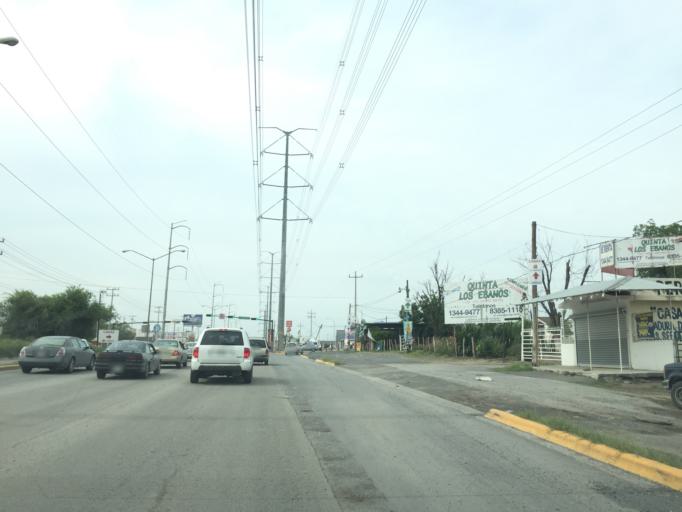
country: MX
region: Nuevo Leon
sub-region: Apodaca
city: Fraccionamiento Cosmopolis Octavo Sector
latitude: 25.8001
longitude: -100.2238
